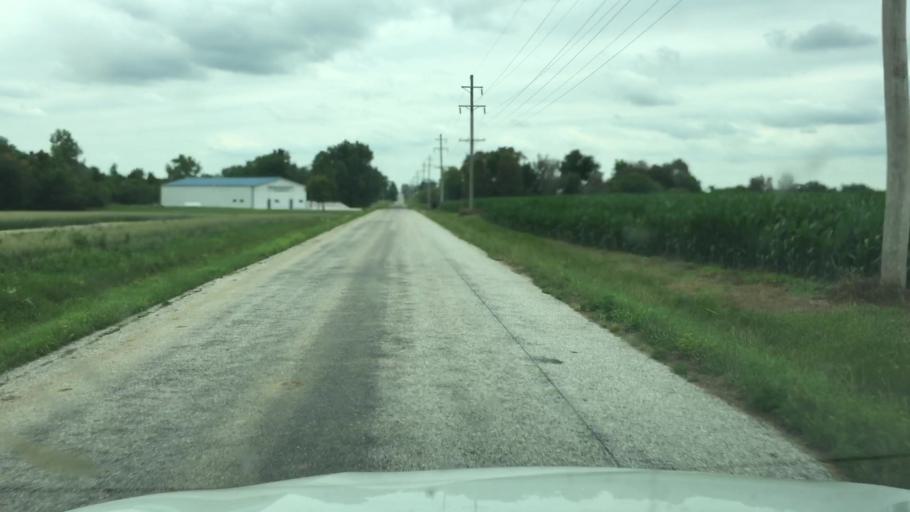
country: US
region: Illinois
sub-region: Hancock County
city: Carthage
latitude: 40.3336
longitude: -91.0825
